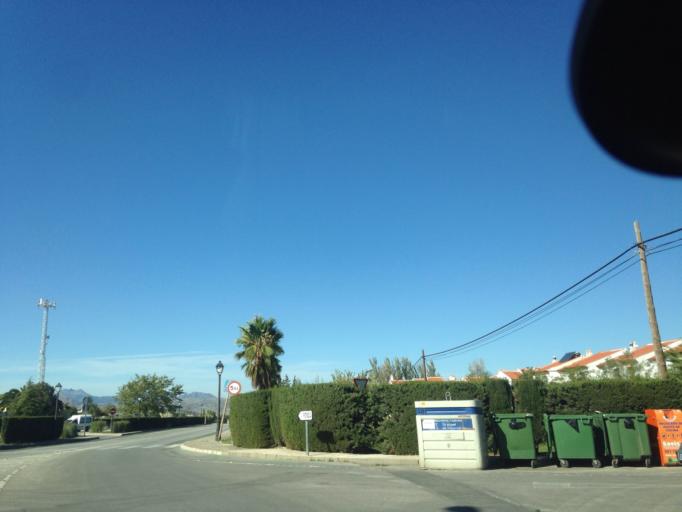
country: ES
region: Andalusia
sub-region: Provincia de Malaga
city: Ronda
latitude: 36.7277
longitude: -5.1522
